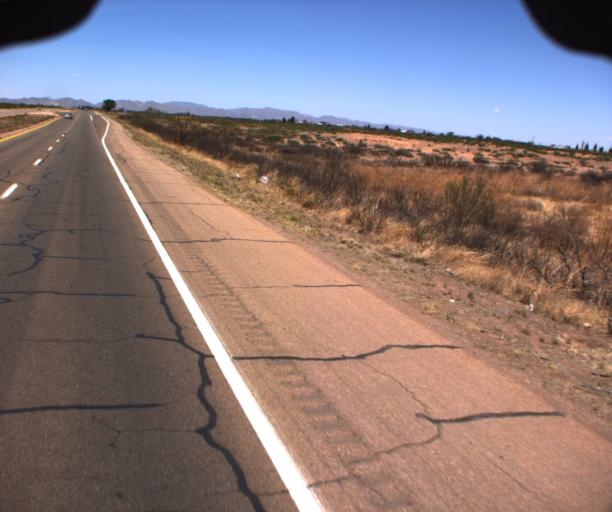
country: US
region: Arizona
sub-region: Cochise County
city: Pirtleville
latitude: 31.3532
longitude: -109.5869
